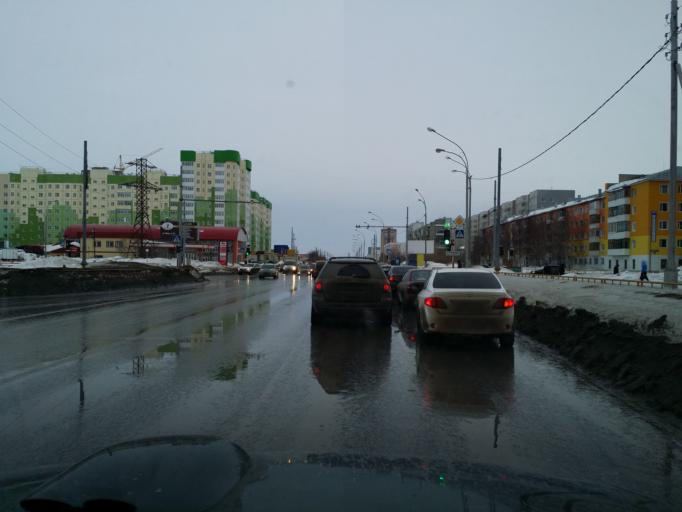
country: RU
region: Khanty-Mansiyskiy Avtonomnyy Okrug
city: Nizhnevartovsk
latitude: 60.9350
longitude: 76.6131
